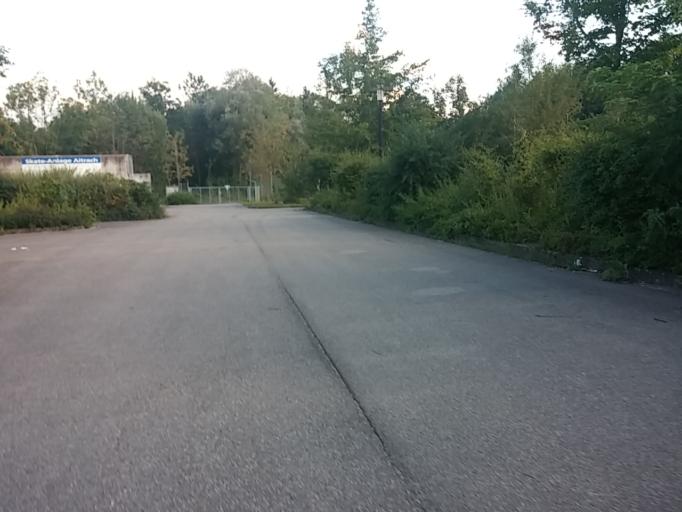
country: DE
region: Baden-Wuerttemberg
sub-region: Tuebingen Region
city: Aitrach
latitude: 47.9349
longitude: 10.0848
